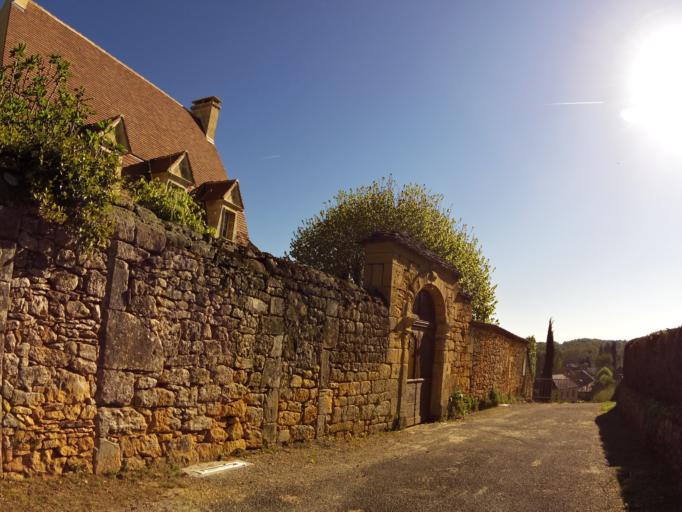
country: FR
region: Midi-Pyrenees
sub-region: Departement du Lot
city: Gourdon
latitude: 44.7981
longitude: 1.3476
